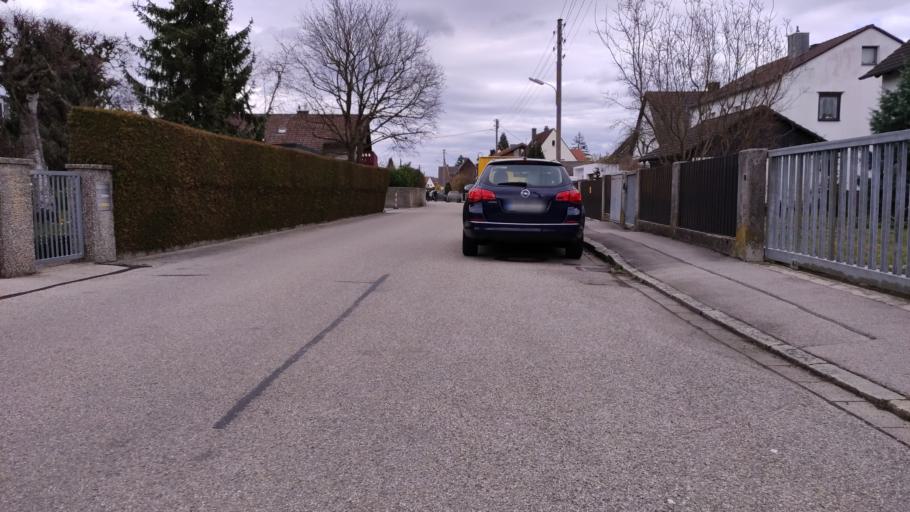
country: DE
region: Bavaria
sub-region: Upper Bavaria
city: Emmering
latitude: 48.1788
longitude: 11.2787
